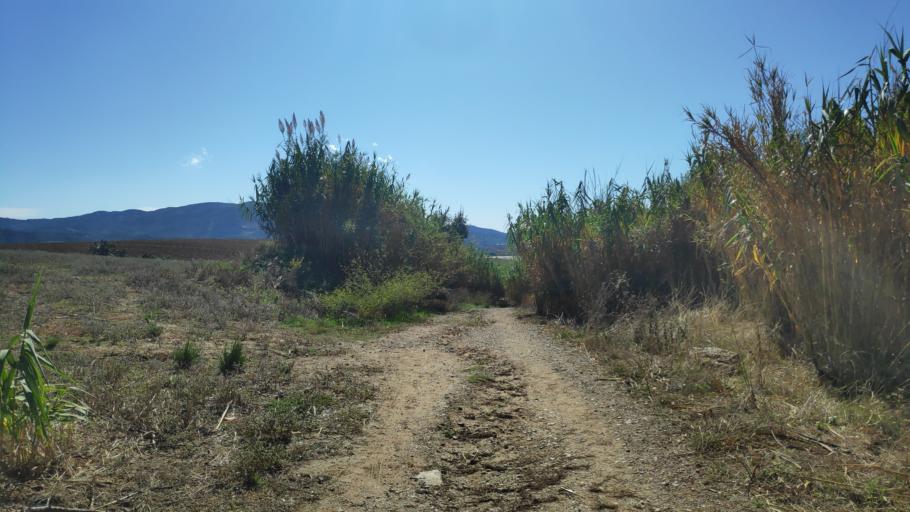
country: ES
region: Catalonia
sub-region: Provincia de Barcelona
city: Santa Perpetua de Mogoda
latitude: 41.5427
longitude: 2.1911
